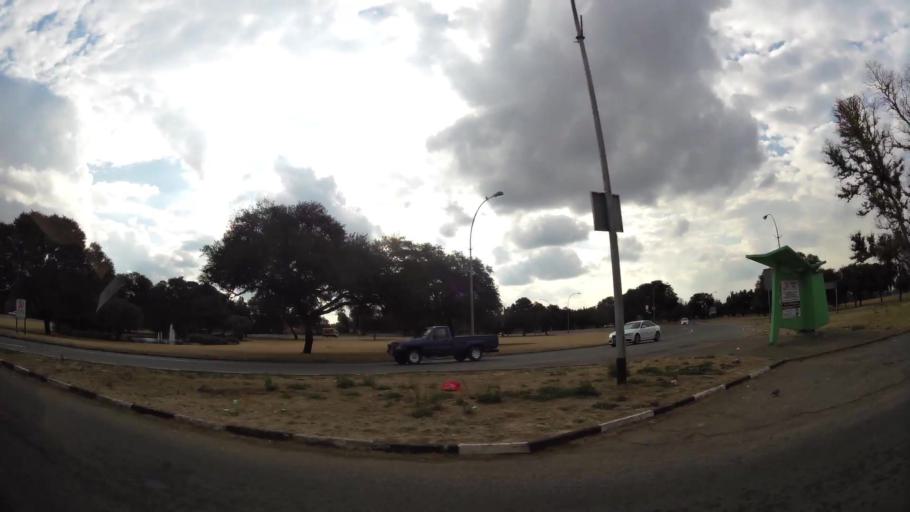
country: ZA
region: Orange Free State
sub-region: Fezile Dabi District Municipality
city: Sasolburg
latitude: -26.8046
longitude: 27.8310
